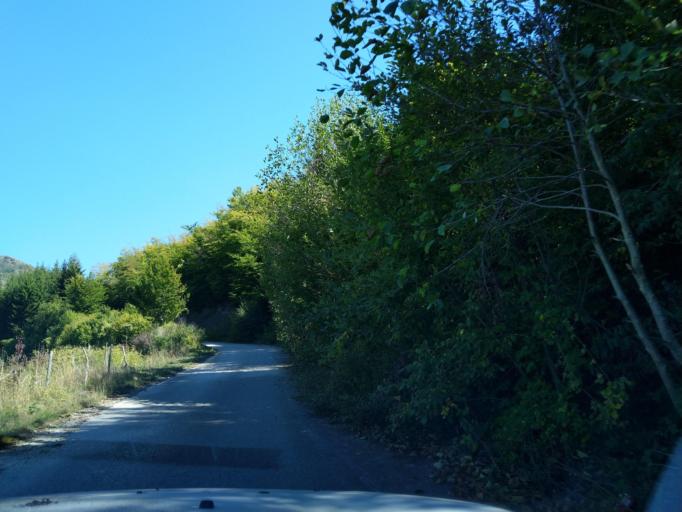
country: RS
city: Sokolovica
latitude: 43.2554
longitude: 20.3055
